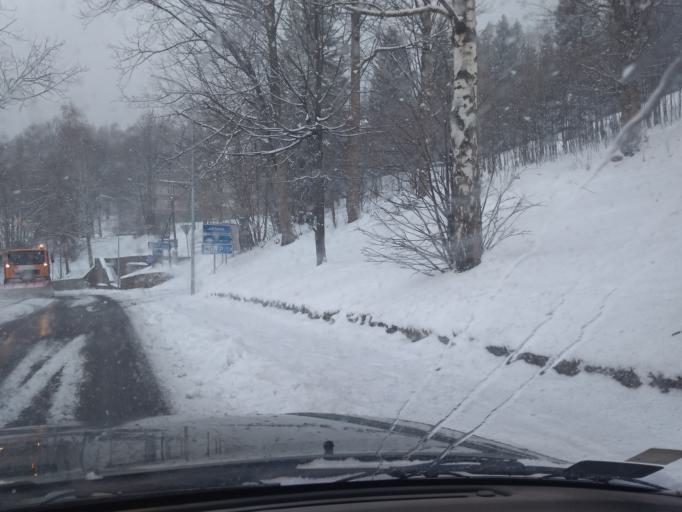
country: PL
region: Lower Silesian Voivodeship
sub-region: Powiat jeleniogorski
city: Karpacz
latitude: 50.7754
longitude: 15.7267
